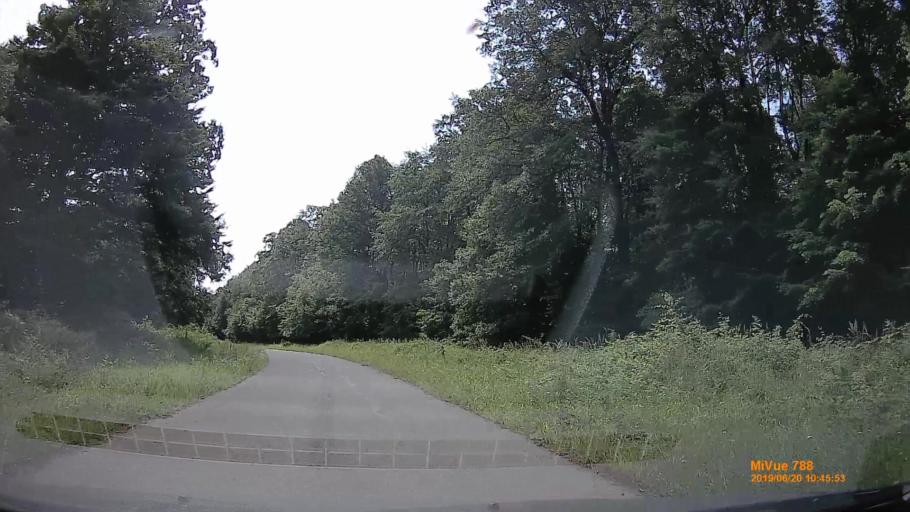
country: HU
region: Baranya
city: Hidas
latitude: 46.1809
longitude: 18.5739
